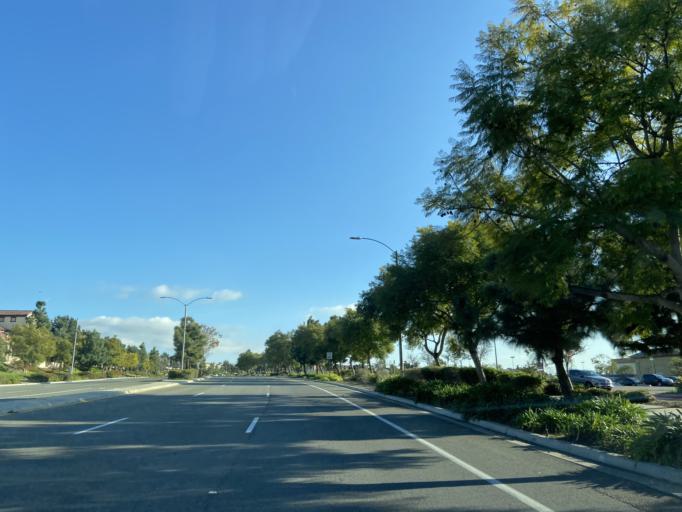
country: US
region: California
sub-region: San Diego County
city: Bonita
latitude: 32.6327
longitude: -116.9670
